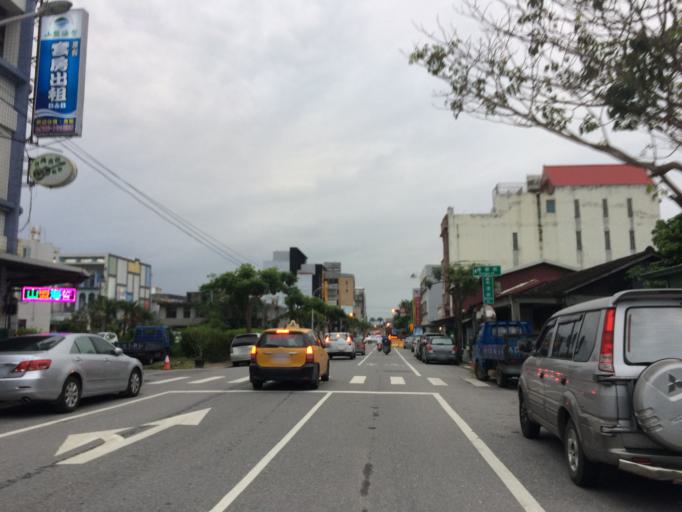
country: TW
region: Taiwan
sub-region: Hualien
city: Hualian
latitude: 23.9745
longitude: 121.6146
